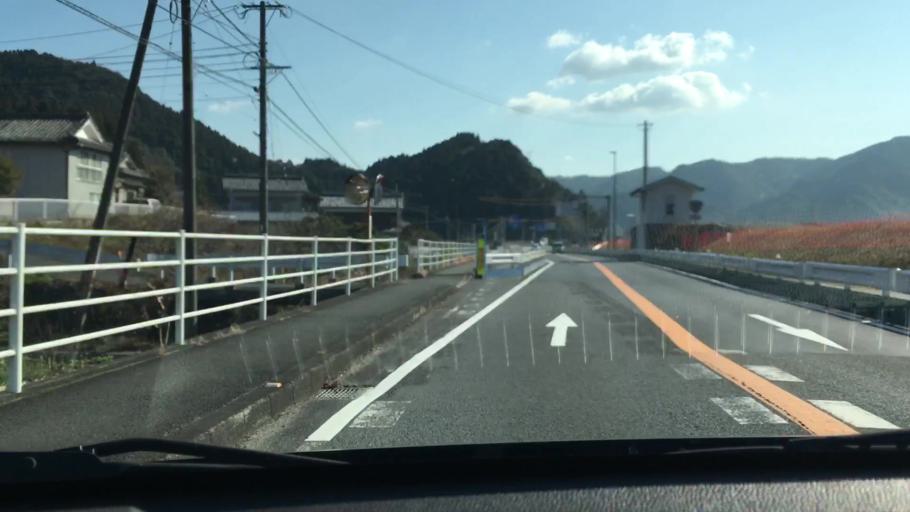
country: JP
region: Oita
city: Saiki
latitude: 32.9595
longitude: 131.8422
